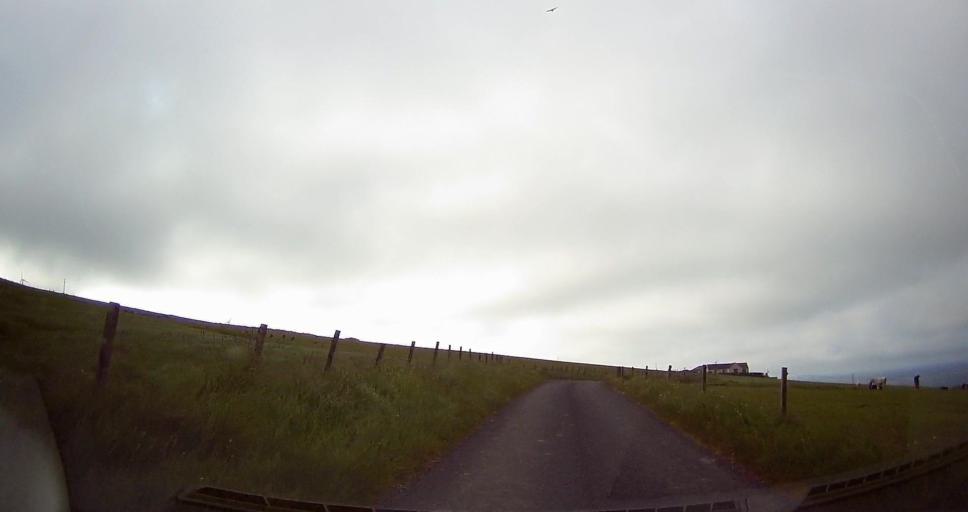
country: GB
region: Scotland
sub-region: Orkney Islands
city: Orkney
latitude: 59.1180
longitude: -3.1315
